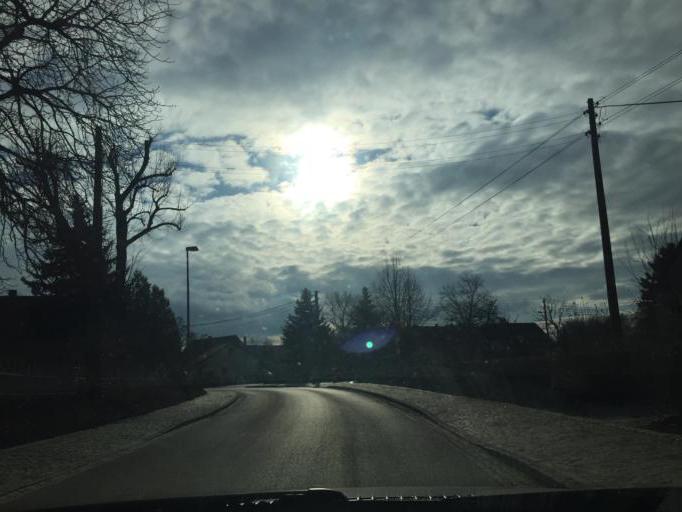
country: DE
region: Saxony
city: Ebersbach
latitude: 51.2341
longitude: 13.6579
